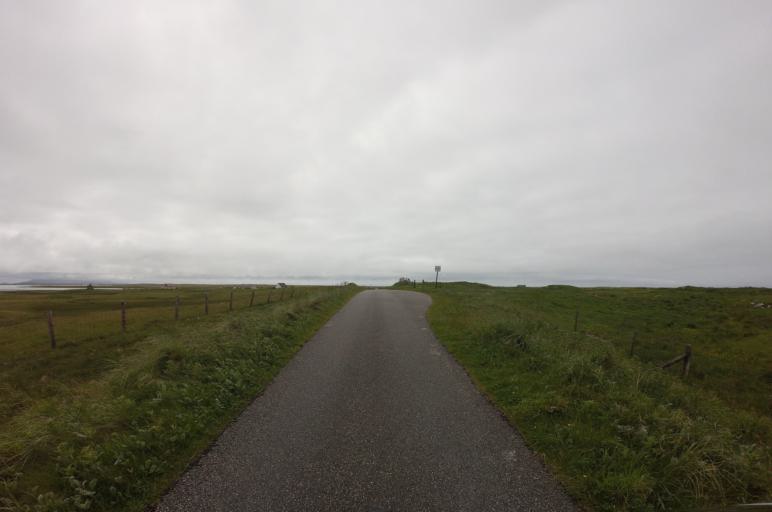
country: GB
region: Scotland
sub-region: Eilean Siar
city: Isle of North Uist
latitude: 57.5315
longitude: -7.3568
